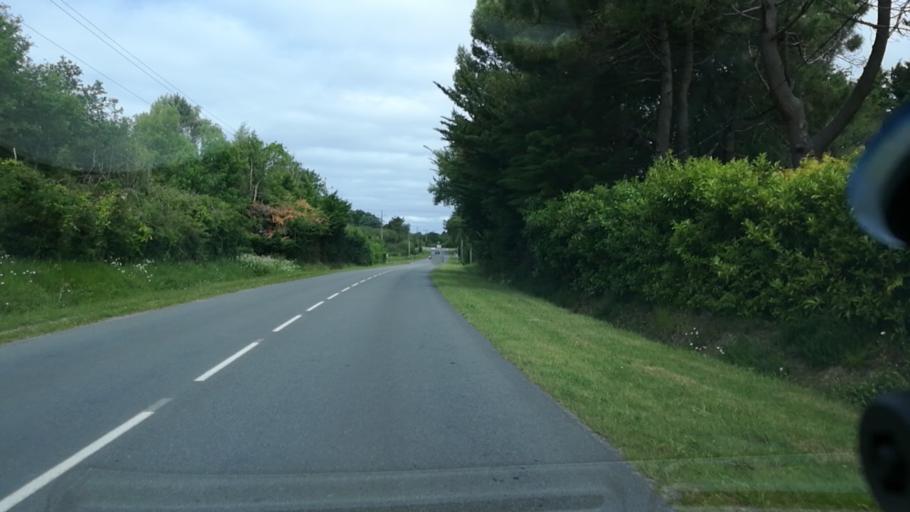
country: FR
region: Brittany
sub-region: Departement du Morbihan
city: Penestin
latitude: 47.4534
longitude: -2.4622
